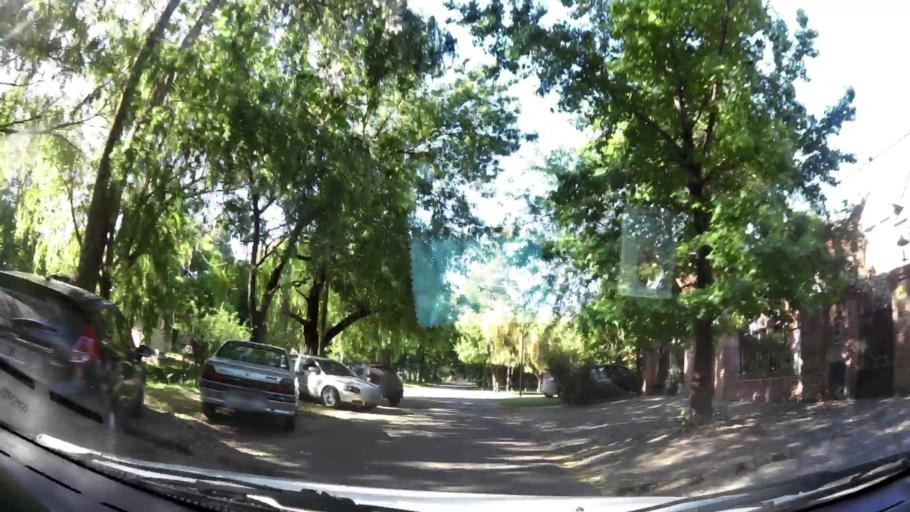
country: AR
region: Buenos Aires
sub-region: Partido de San Isidro
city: San Isidro
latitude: -34.4801
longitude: -58.5425
